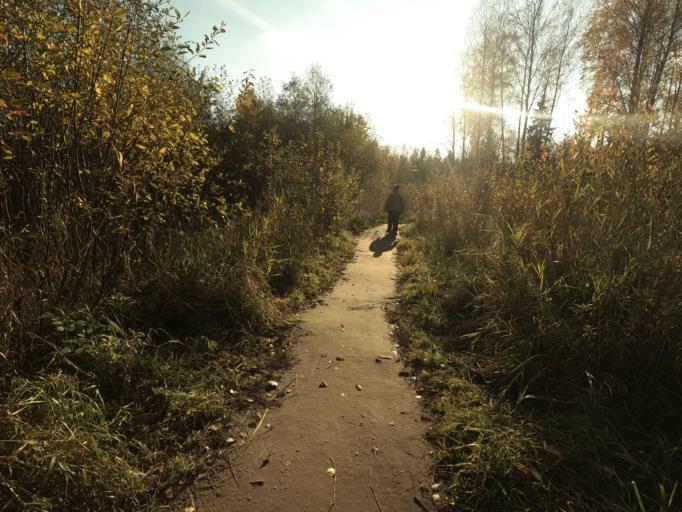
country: RU
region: Leningrad
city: Sertolovo
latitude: 60.1454
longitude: 30.2382
